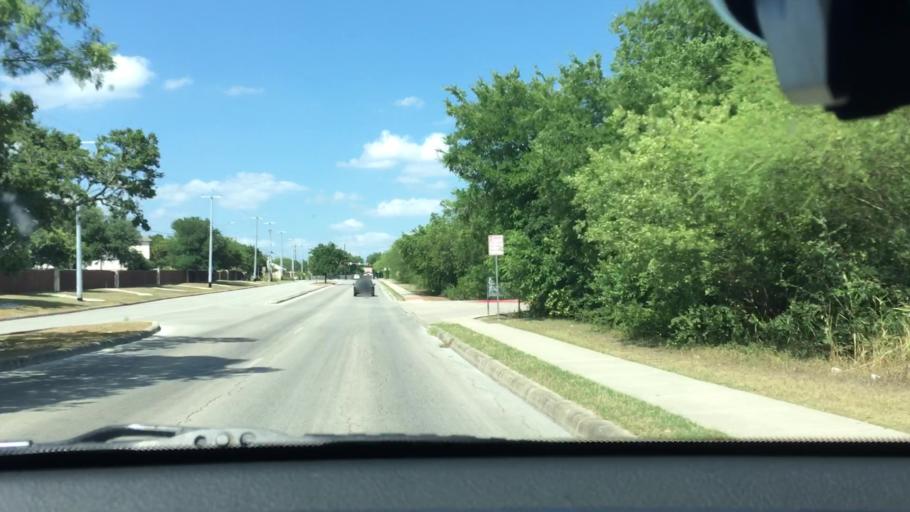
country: US
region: Texas
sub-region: Bexar County
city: Live Oak
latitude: 29.5961
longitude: -98.3875
